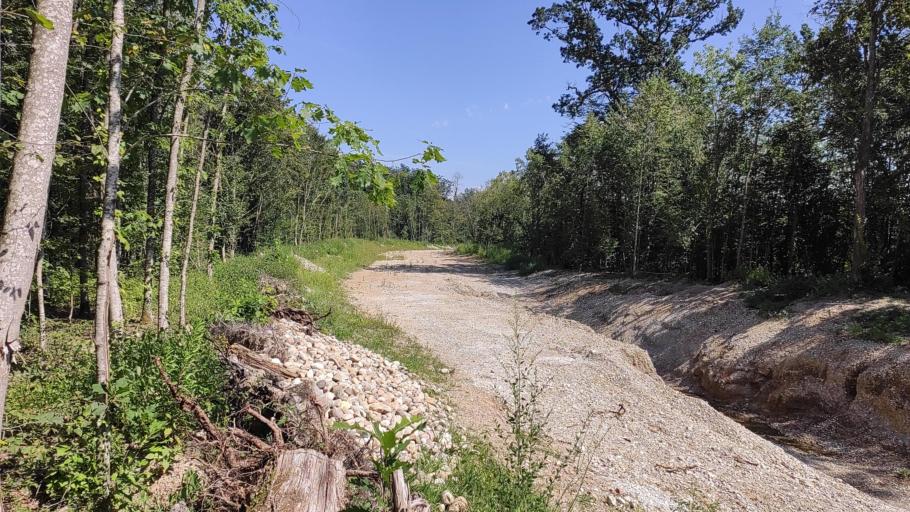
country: DE
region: Baden-Wuerttemberg
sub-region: Freiburg Region
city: Merdingen
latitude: 48.0008
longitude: 7.6547
